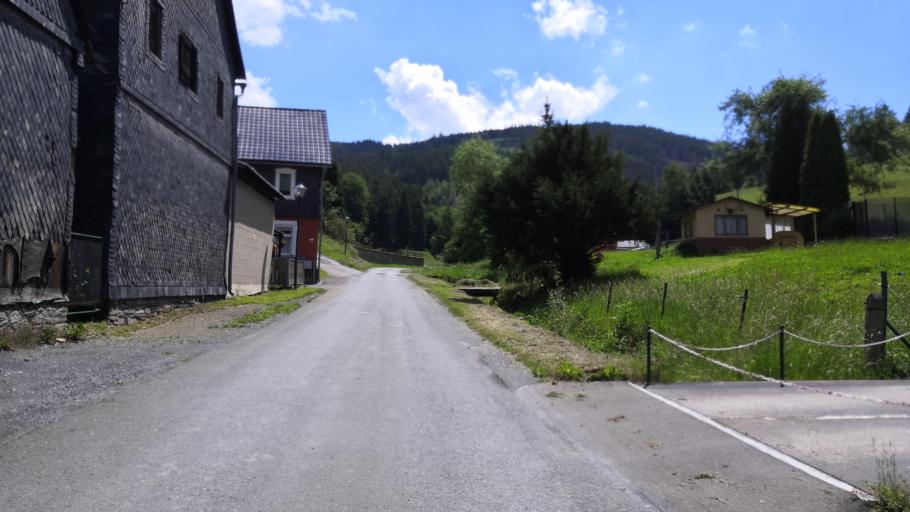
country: DE
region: Thuringia
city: Probstzella
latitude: 50.5661
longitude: 11.3770
